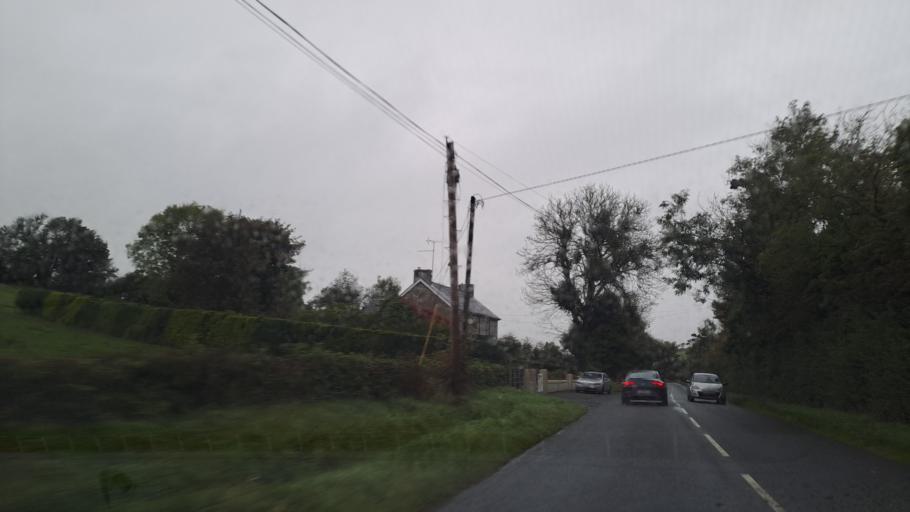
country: IE
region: Ulster
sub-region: County Monaghan
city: Monaghan
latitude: 54.2192
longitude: -6.9178
